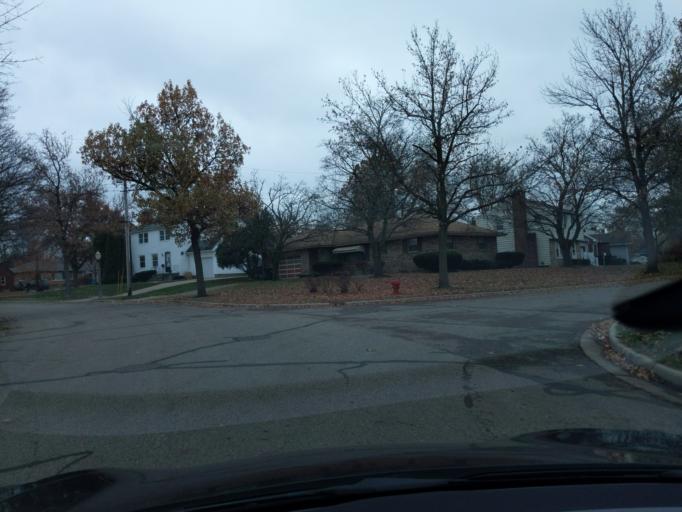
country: US
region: Michigan
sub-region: Ingham County
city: Lansing
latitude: 42.7069
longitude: -84.5809
